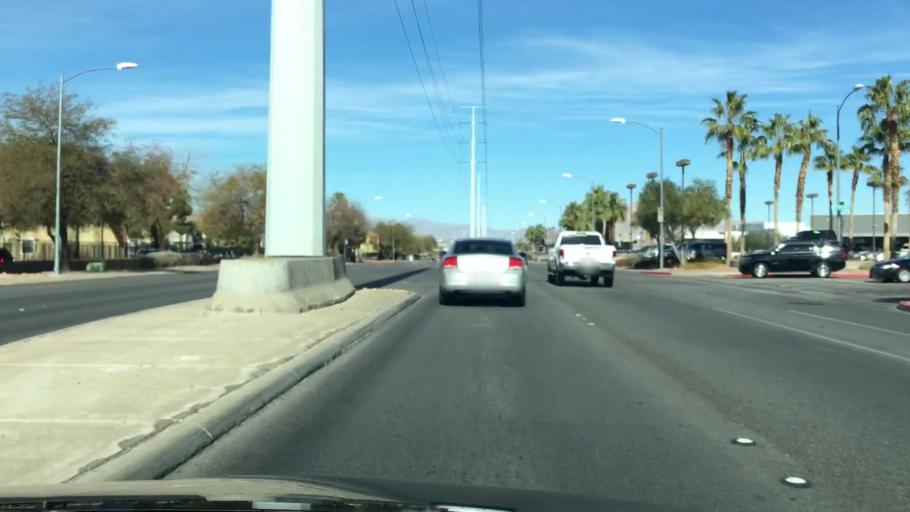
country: US
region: Nevada
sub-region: Clark County
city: Henderson
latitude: 36.0496
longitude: -115.0290
